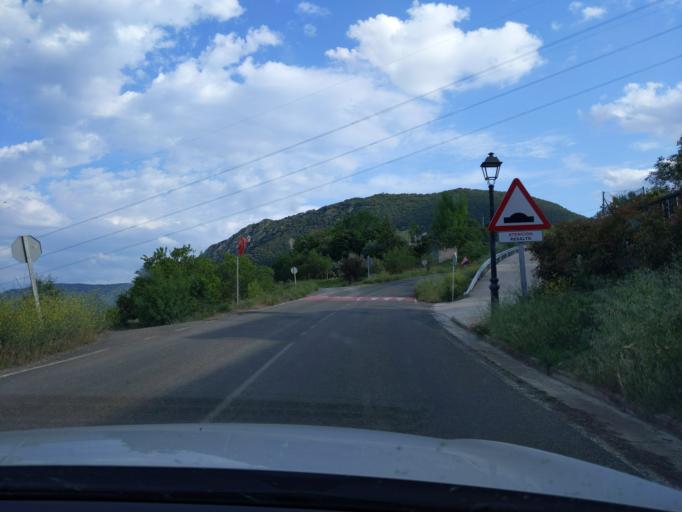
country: ES
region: La Rioja
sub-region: Provincia de La Rioja
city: Clavijo
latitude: 42.3654
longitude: -2.4209
